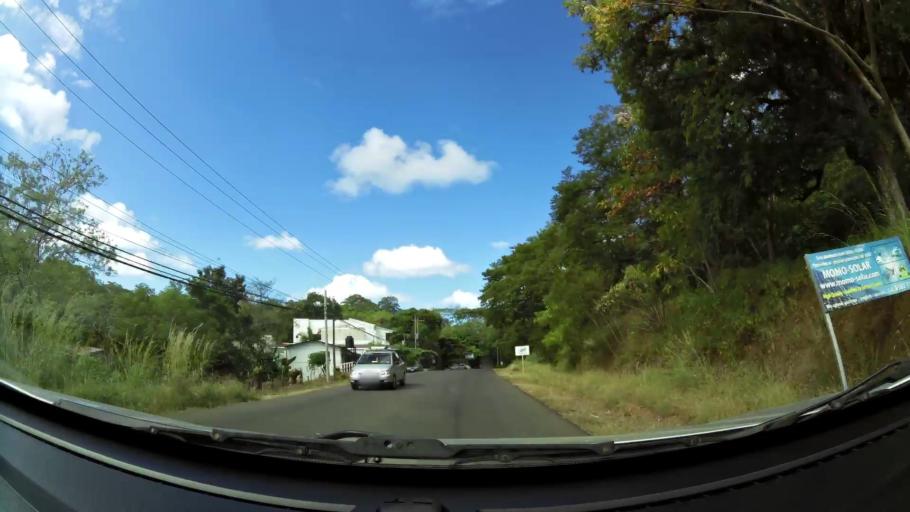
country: CR
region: Guanacaste
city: Santa Cruz
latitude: 10.3091
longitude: -85.8108
